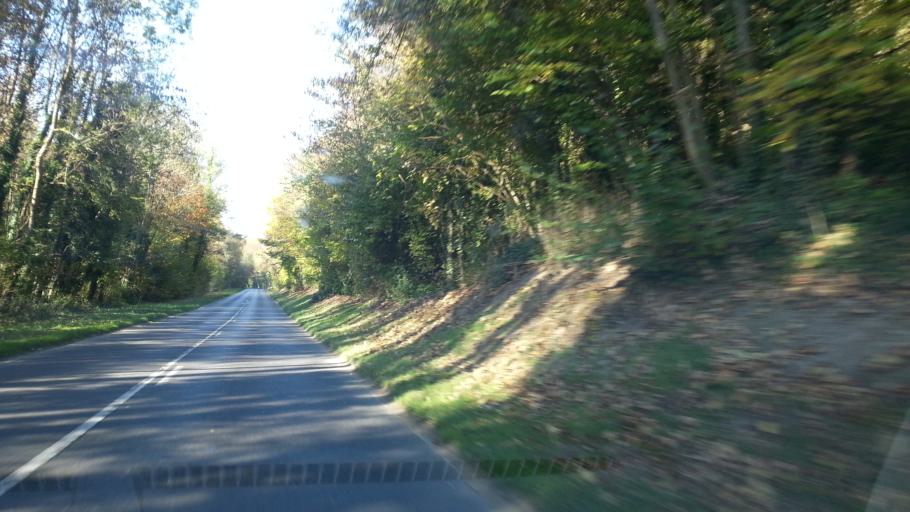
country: FR
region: Picardie
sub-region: Departement de l'Oise
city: Thiverny
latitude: 49.2627
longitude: 2.4057
